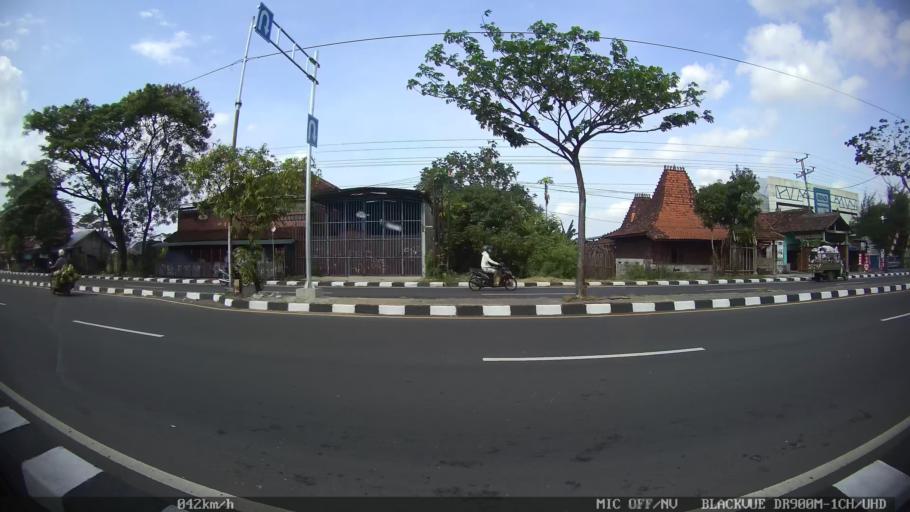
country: ID
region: Daerah Istimewa Yogyakarta
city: Kasihan
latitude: -7.8335
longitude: 110.3608
